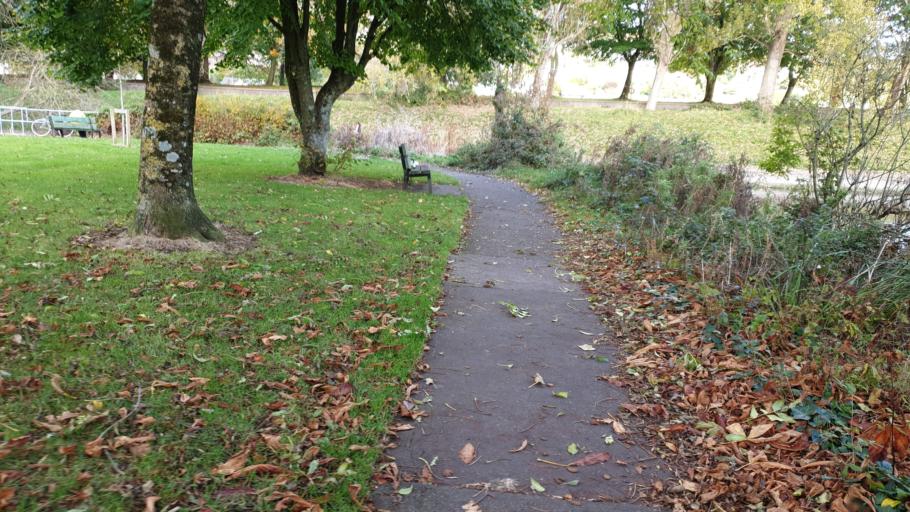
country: IE
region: Munster
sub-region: County Cork
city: Cork
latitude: 51.9001
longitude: -8.4327
